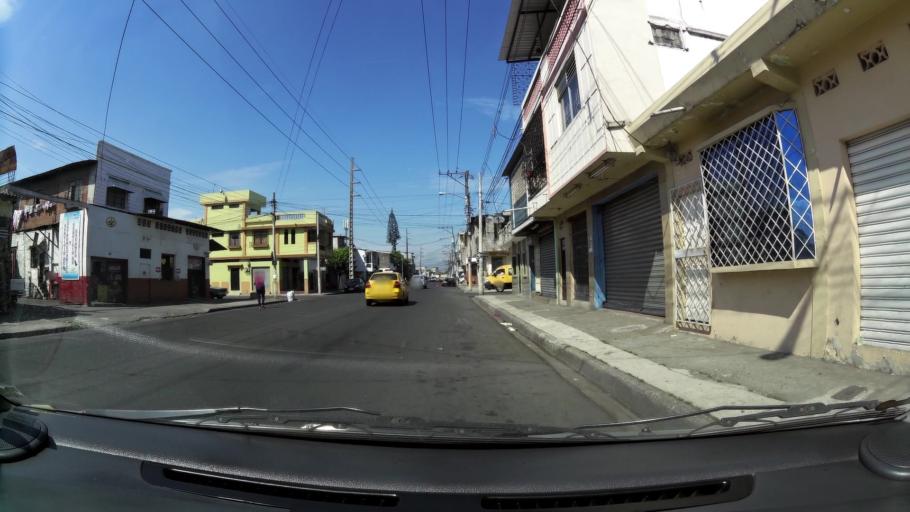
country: EC
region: Guayas
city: Guayaquil
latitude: -2.2102
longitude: -79.9096
